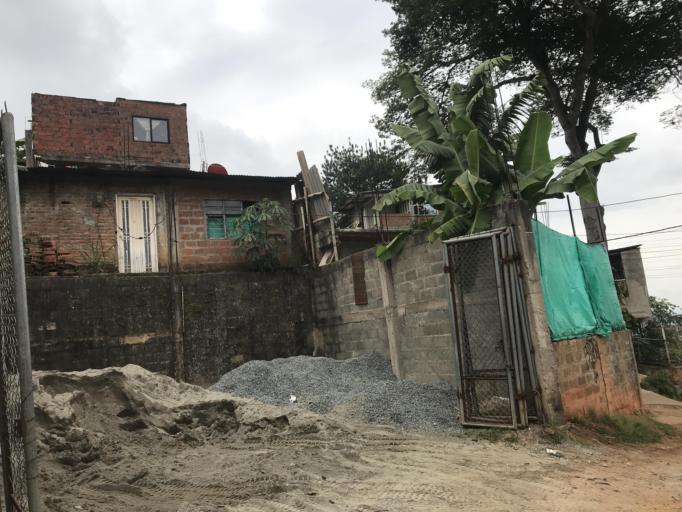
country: CO
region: Valle del Cauca
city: Cali
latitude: 3.3756
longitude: -76.5582
